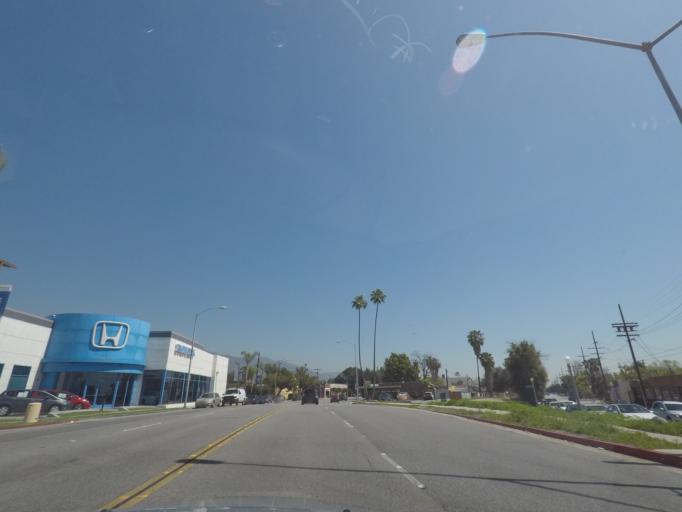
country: US
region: California
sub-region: Los Angeles County
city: East Pasadena
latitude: 34.1497
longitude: -118.1103
